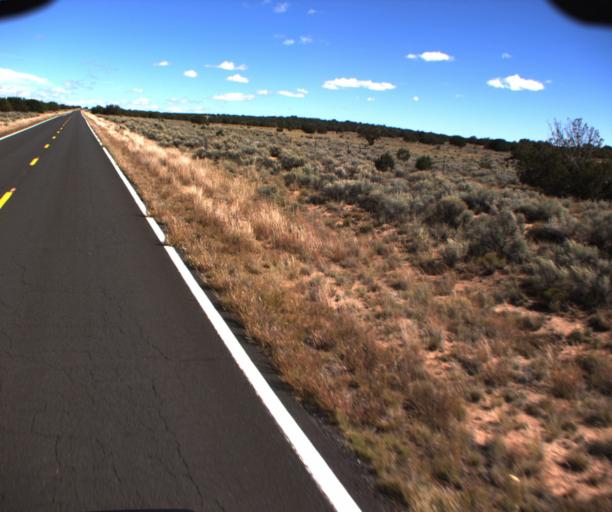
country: US
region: Arizona
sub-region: Apache County
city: Houck
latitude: 34.9138
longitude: -109.2195
